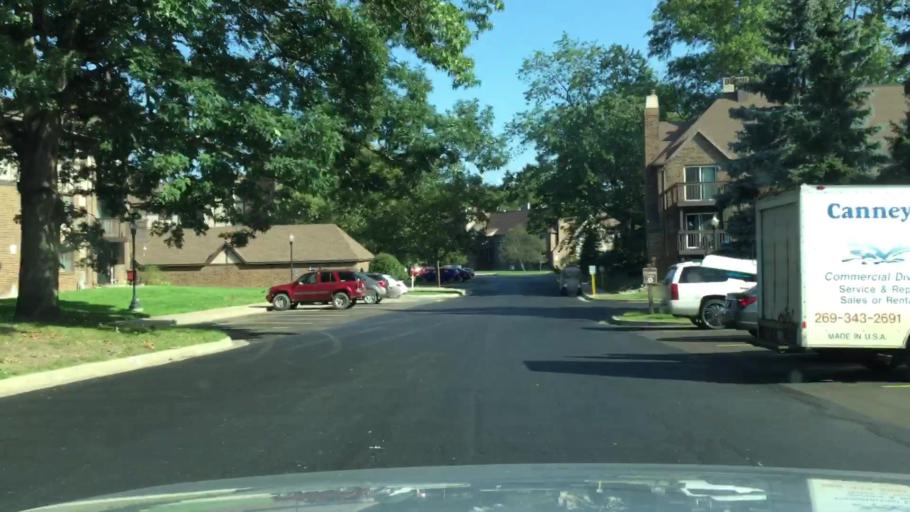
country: US
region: Michigan
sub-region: Kalamazoo County
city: Portage
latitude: 42.2455
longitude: -85.5832
